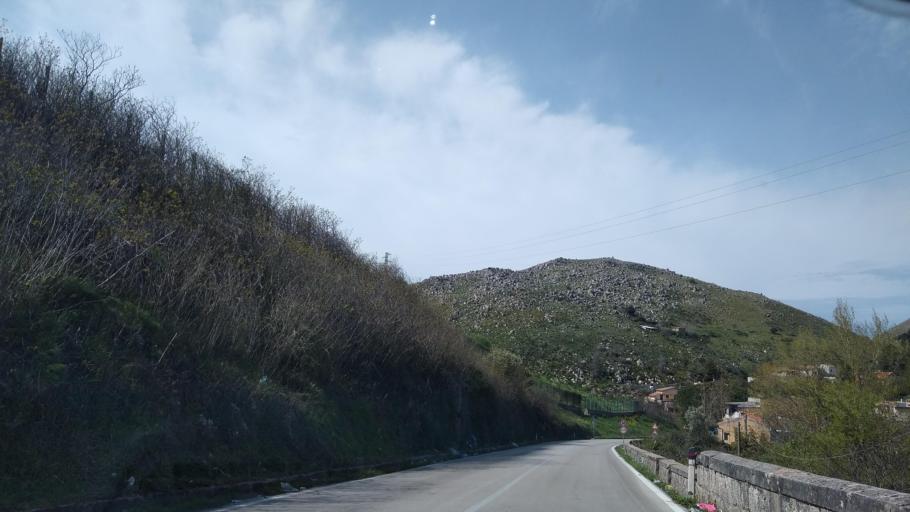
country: IT
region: Sicily
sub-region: Palermo
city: Pioppo
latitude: 38.0462
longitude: 13.1979
